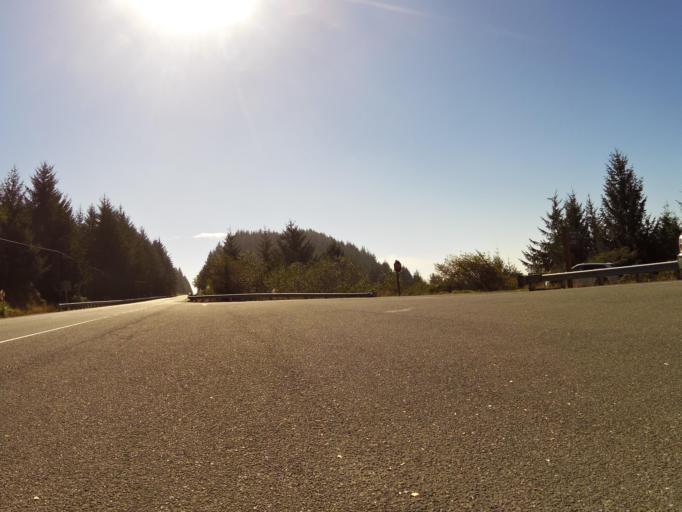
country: US
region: Oregon
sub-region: Curry County
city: Brookings
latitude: 42.1002
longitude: -124.3398
